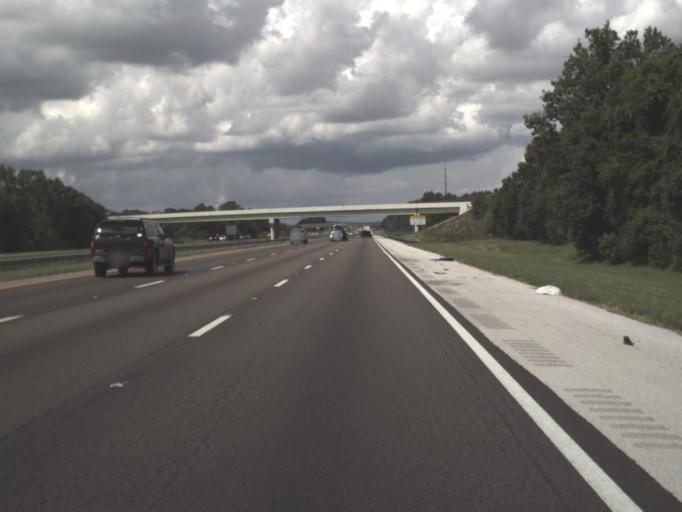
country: US
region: Florida
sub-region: Hillsborough County
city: Ruskin
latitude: 27.6997
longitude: -82.4002
